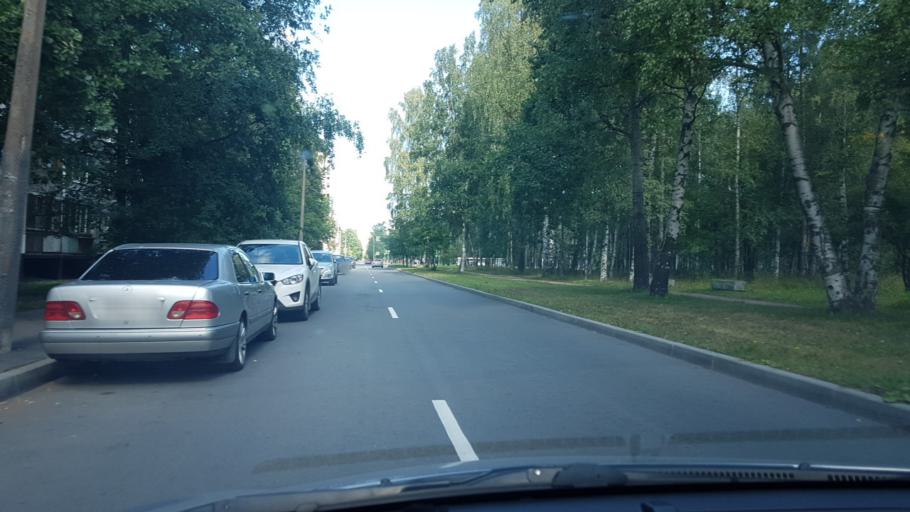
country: RU
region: St.-Petersburg
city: Dachnoye
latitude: 59.8335
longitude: 30.2242
